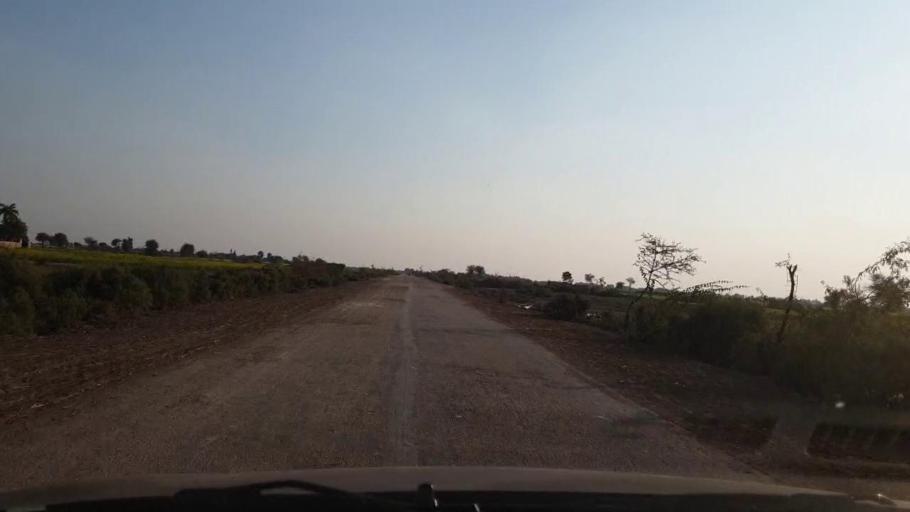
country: PK
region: Sindh
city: Jhol
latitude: 25.9273
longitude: 68.9081
